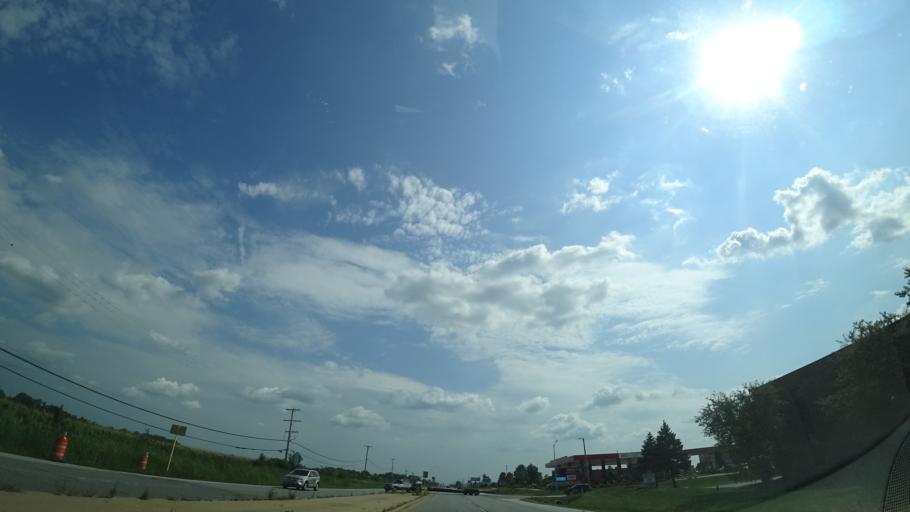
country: US
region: Illinois
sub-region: Will County
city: Frankfort Square
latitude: 41.5379
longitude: -87.7904
